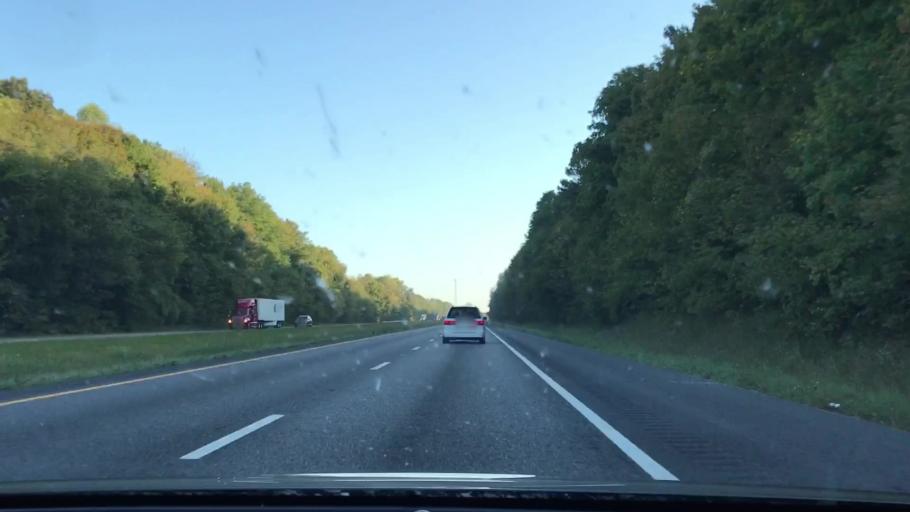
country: US
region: Tennessee
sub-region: Robertson County
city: Cross Plains
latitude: 36.5355
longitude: -86.6398
